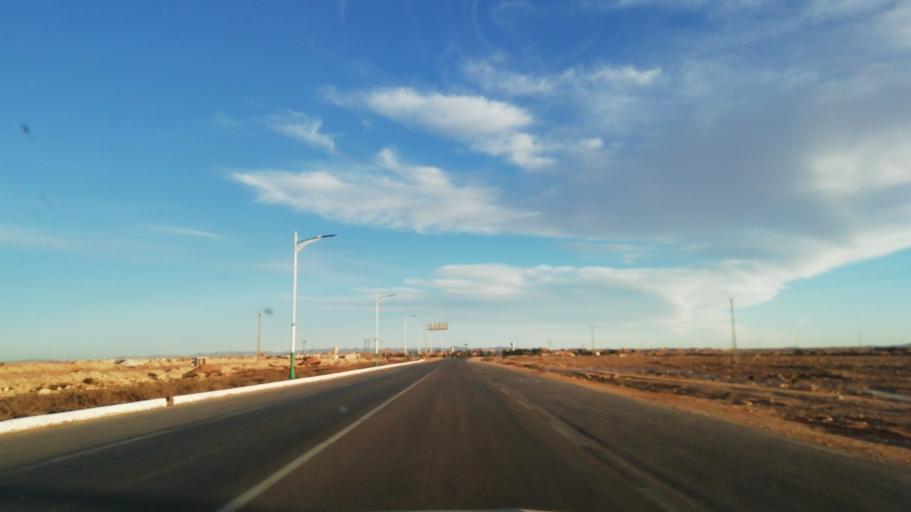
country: DZ
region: Wilaya de Naama
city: Naama
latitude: 33.7251
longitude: -0.7419
